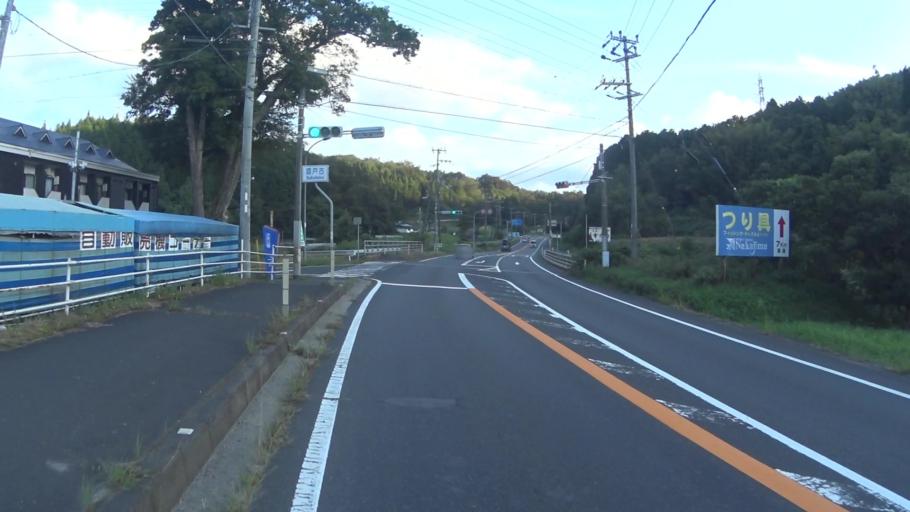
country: JP
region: Kyoto
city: Miyazu
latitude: 35.5608
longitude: 135.1117
